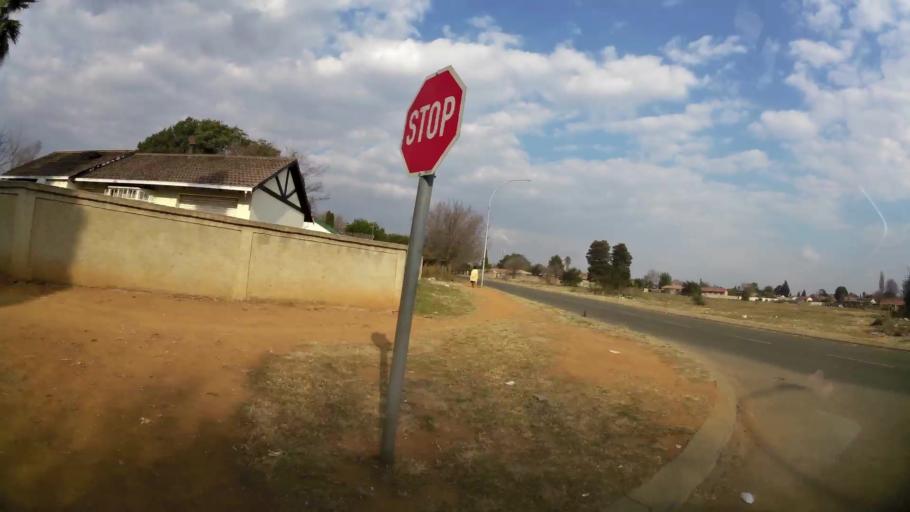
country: ZA
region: Gauteng
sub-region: Ekurhuleni Metropolitan Municipality
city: Benoni
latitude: -26.1192
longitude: 28.3707
